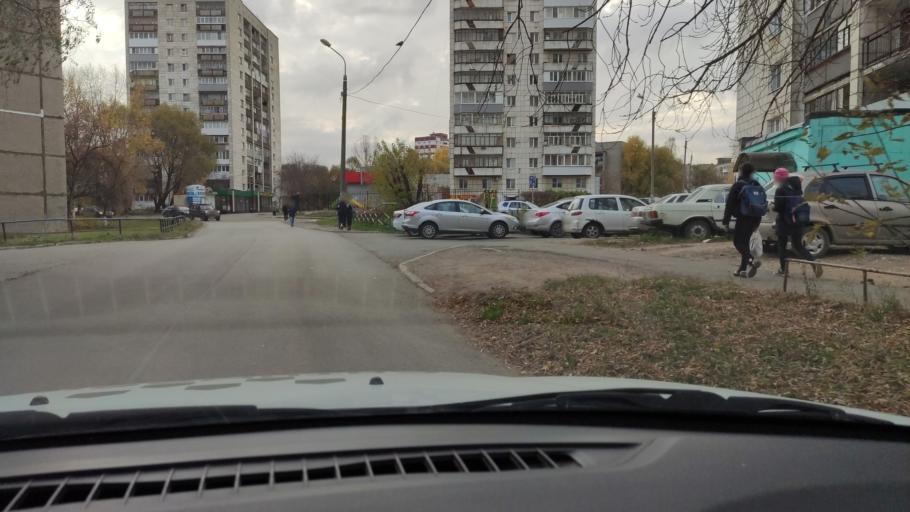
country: RU
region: Perm
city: Perm
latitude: 57.9800
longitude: 56.2324
